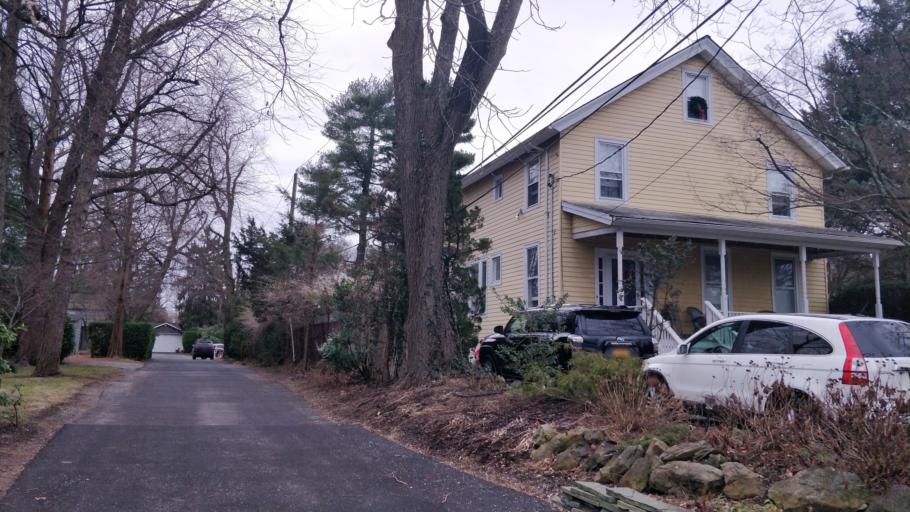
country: US
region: New York
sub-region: Nassau County
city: Glen Cove
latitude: 40.8711
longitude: -73.6315
